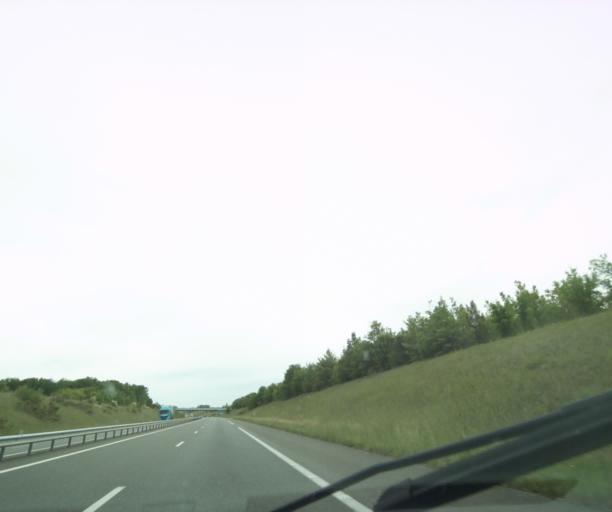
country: FR
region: Midi-Pyrenees
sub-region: Departement du Tarn-et-Garonne
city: Caussade
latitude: 44.2167
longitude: 1.5400
